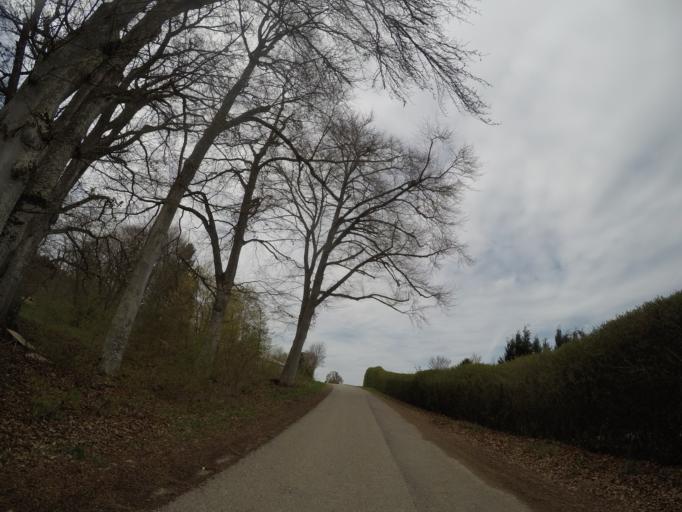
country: DE
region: Baden-Wuerttemberg
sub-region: Tuebingen Region
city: Laichingen
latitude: 48.4780
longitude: 9.6950
